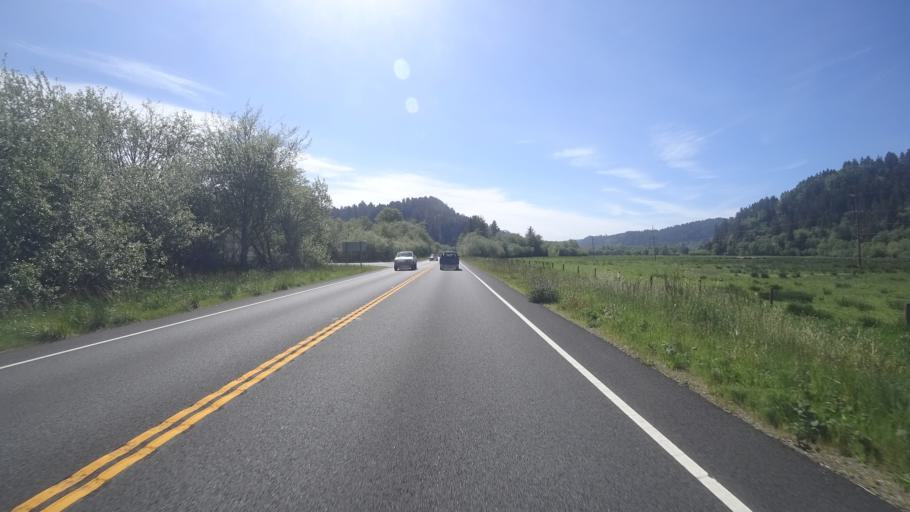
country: US
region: California
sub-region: Del Norte County
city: Bertsch-Oceanview
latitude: 41.5598
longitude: -124.0609
